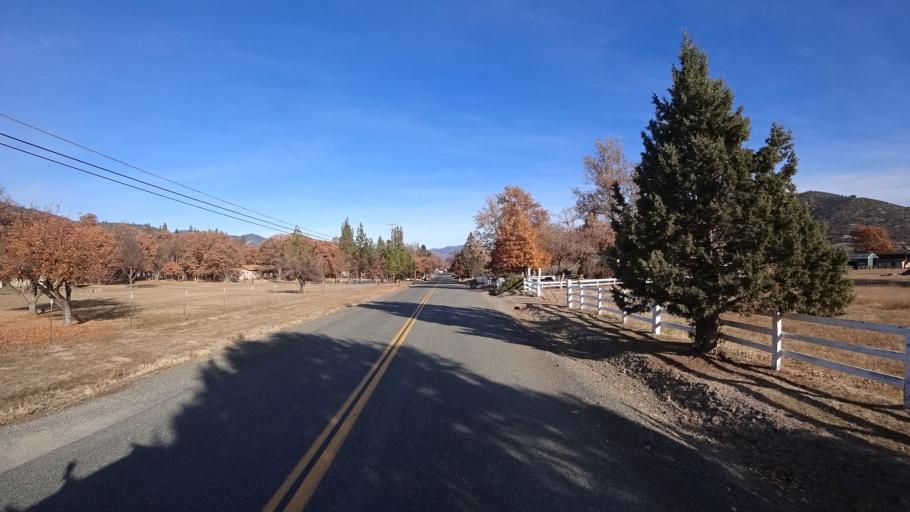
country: US
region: California
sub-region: Siskiyou County
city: Yreka
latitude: 41.6748
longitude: -122.6354
